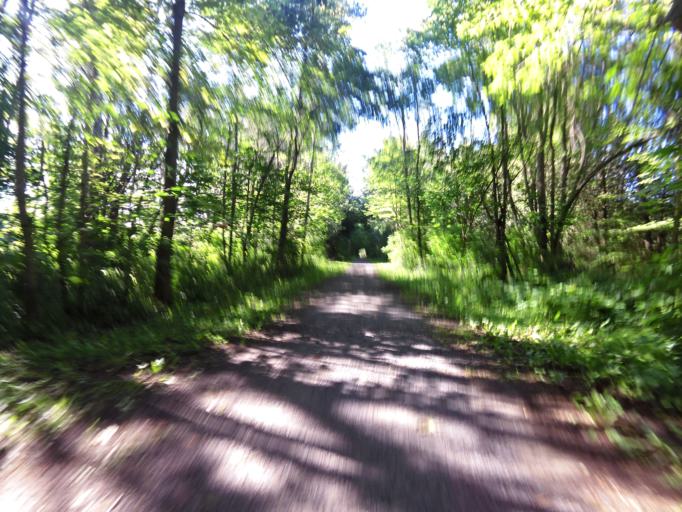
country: CA
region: Ontario
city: Ottawa
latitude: 45.2536
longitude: -75.6217
